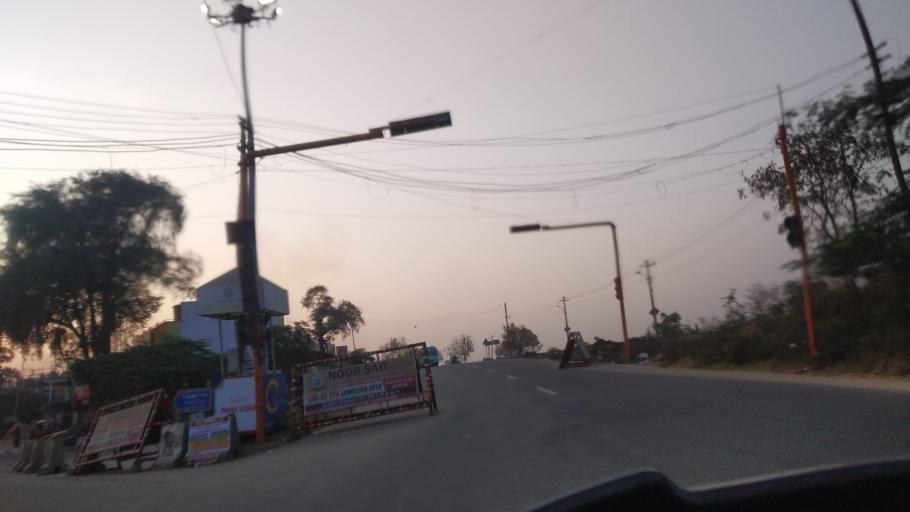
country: IN
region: Tamil Nadu
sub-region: Coimbatore
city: Coimbatore
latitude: 10.9718
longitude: 76.9658
